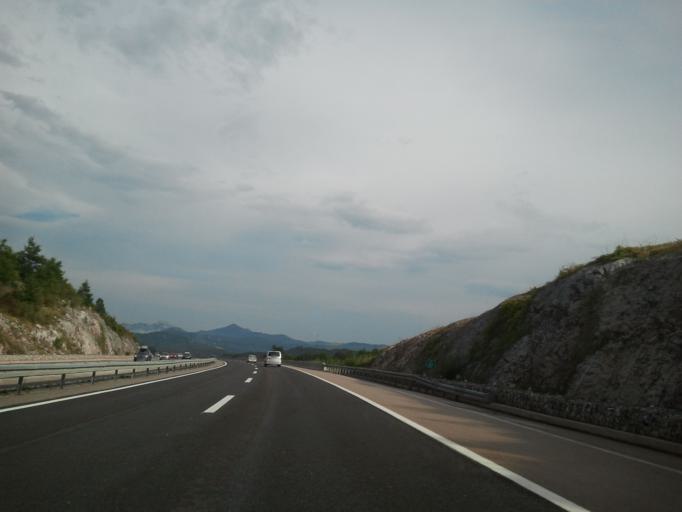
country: HR
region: Zadarska
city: Obrovac
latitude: 44.3349
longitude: 15.6545
